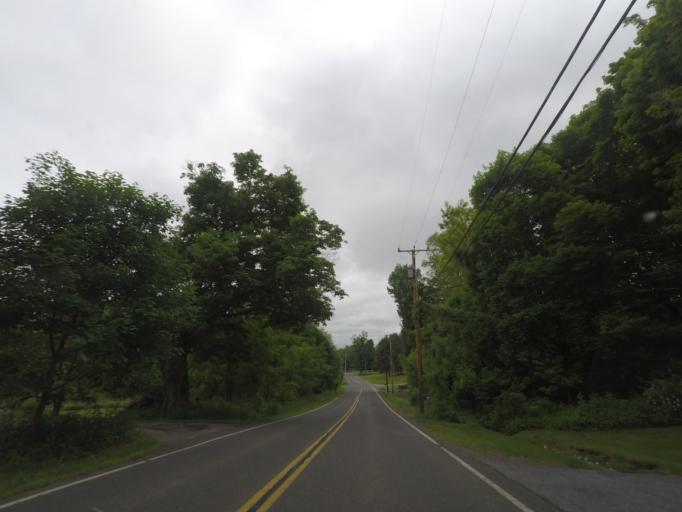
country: US
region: New York
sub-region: Dutchess County
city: Pine Plains
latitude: 41.9614
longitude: -73.5030
